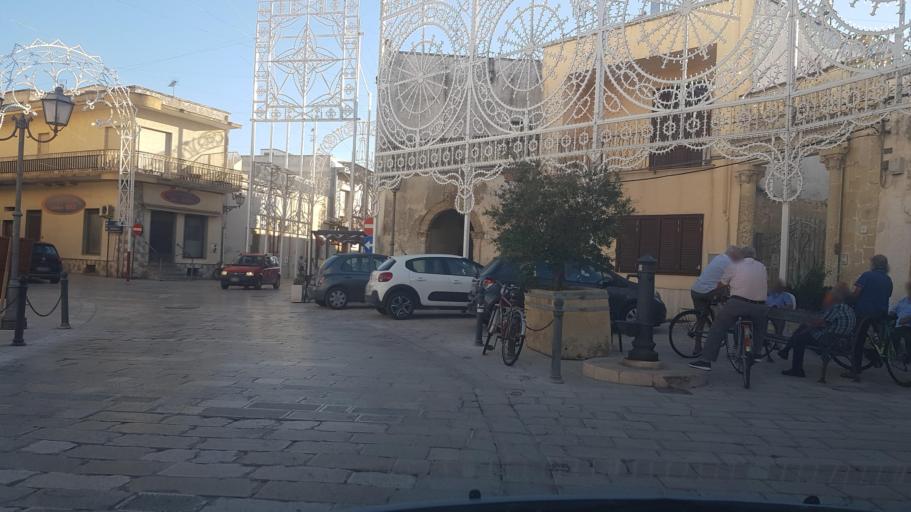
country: IT
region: Apulia
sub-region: Provincia di Lecce
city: Struda
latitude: 40.3206
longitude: 18.2822
